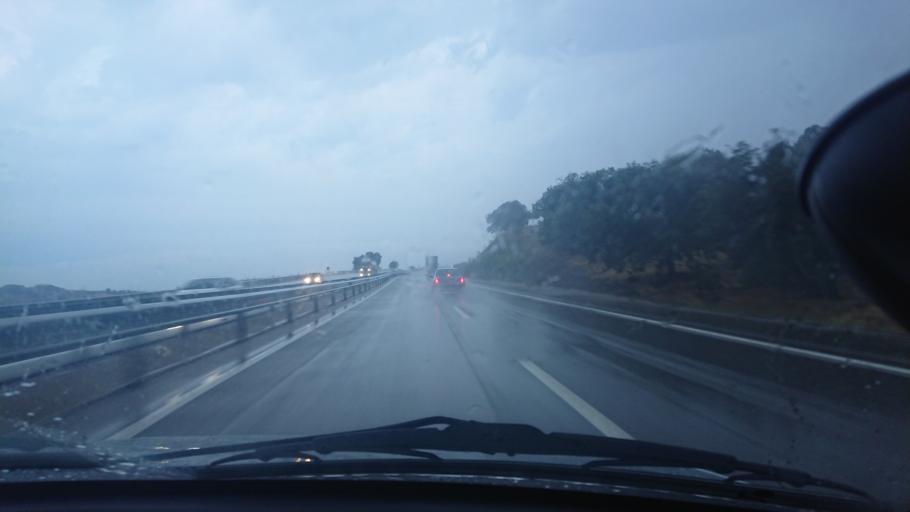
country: TR
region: Manisa
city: Menye
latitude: 38.5322
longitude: 28.4229
